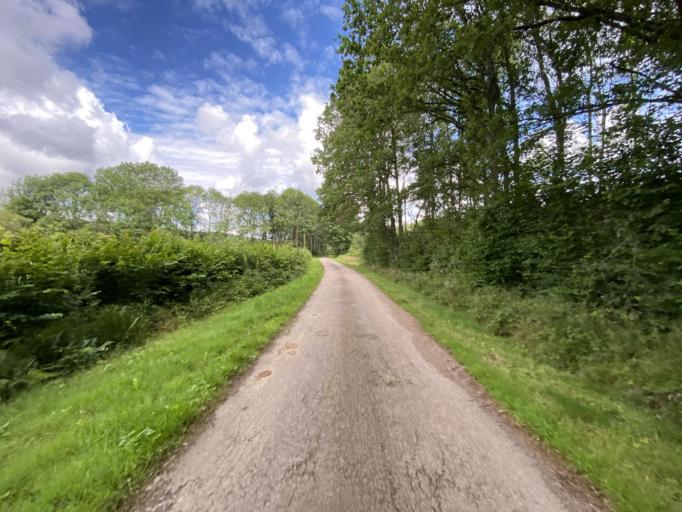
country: FR
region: Bourgogne
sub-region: Departement de la Cote-d'Or
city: Saulieu
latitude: 47.2836
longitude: 4.1762
